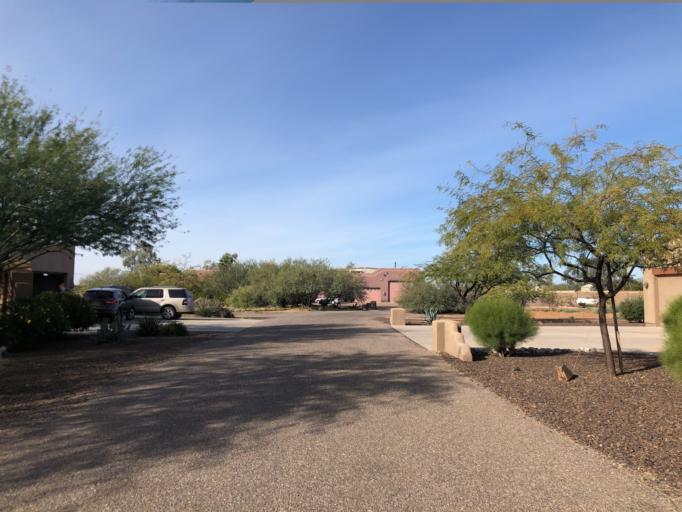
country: US
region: Arizona
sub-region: Maricopa County
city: Anthem
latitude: 33.8322
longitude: -112.0764
